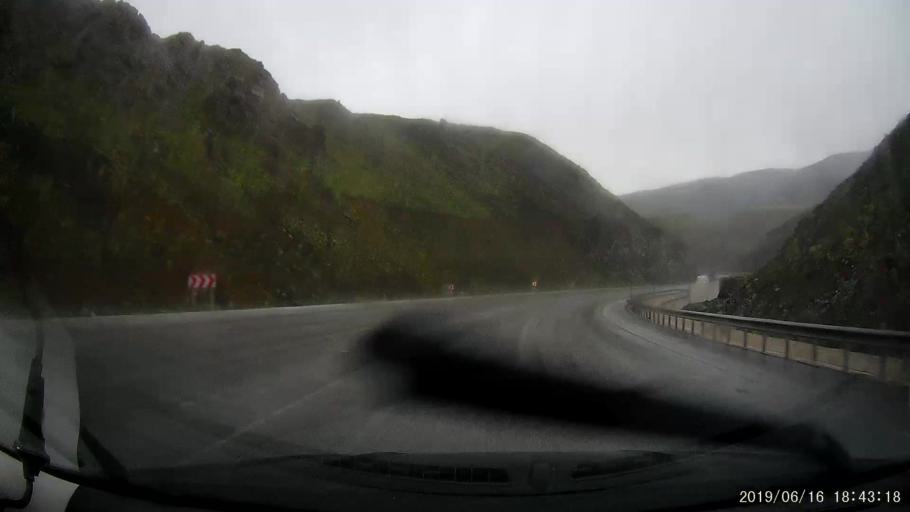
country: TR
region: Erzincan
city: Doganbeyli
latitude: 39.8680
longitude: 39.0924
